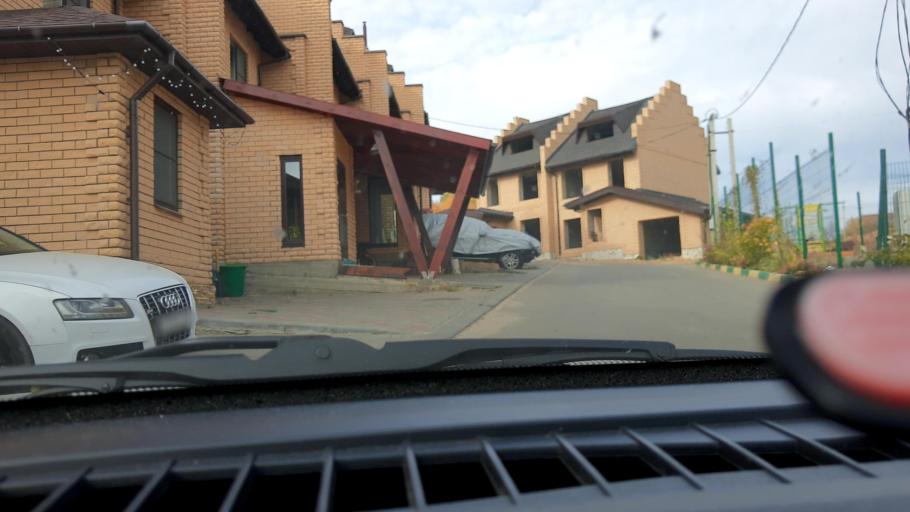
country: RU
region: Nizjnij Novgorod
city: Afonino
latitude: 56.2449
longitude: 44.0789
